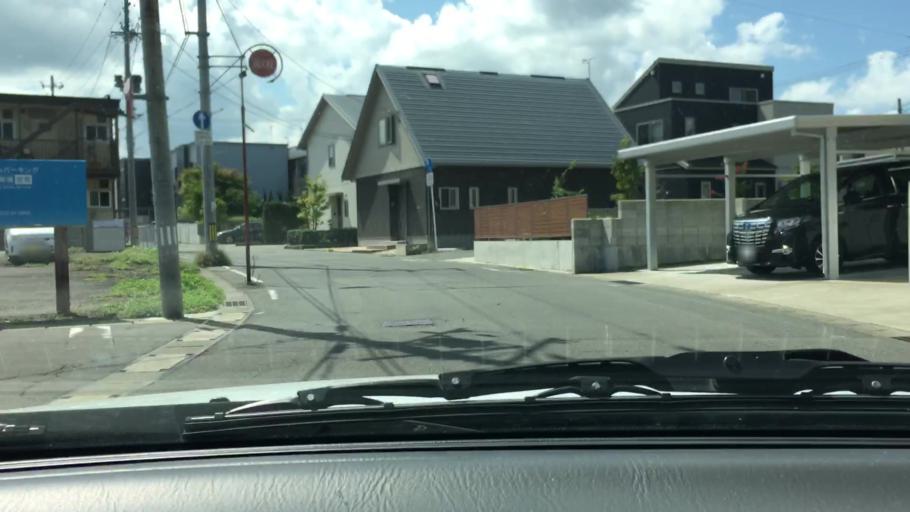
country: JP
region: Aomori
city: Hirosaki
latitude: 40.5930
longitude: 140.4715
